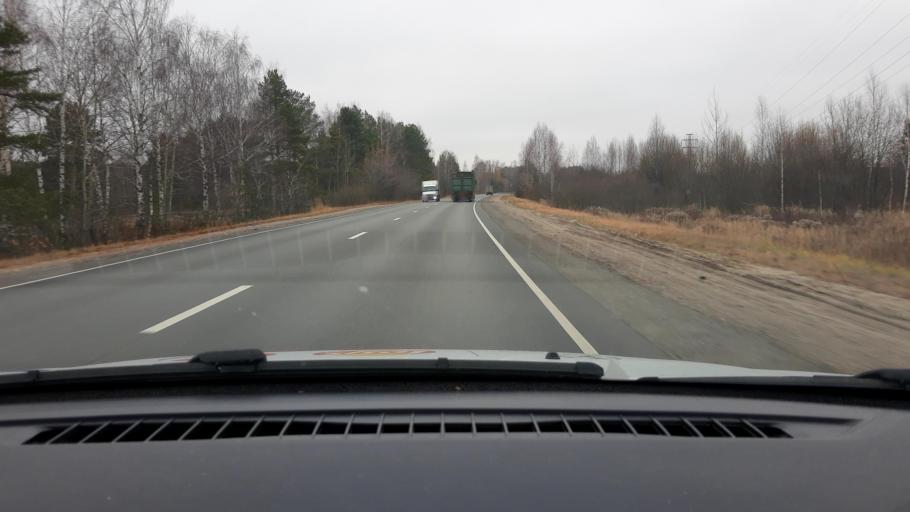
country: RU
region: Nizjnij Novgorod
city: Gidrotorf
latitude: 56.5576
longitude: 43.5019
